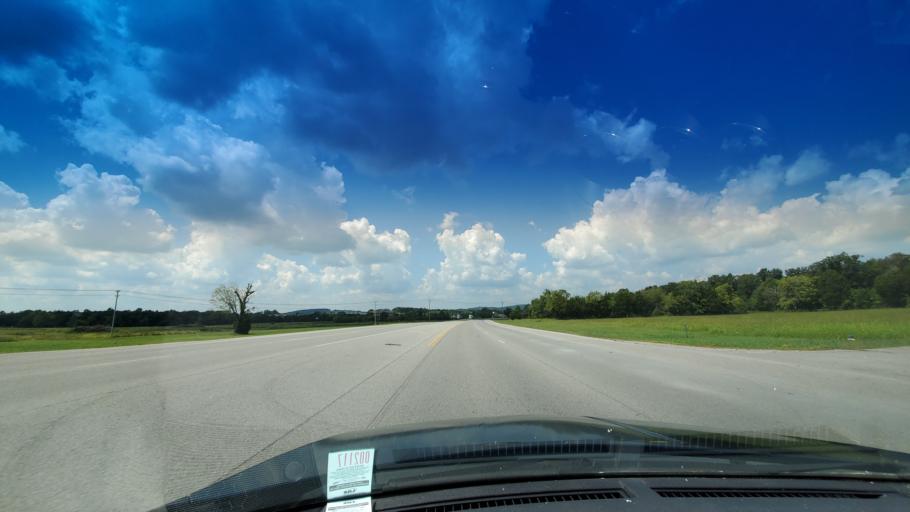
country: US
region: Tennessee
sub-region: Wilson County
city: Lebanon
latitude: 36.1771
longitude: -86.3209
